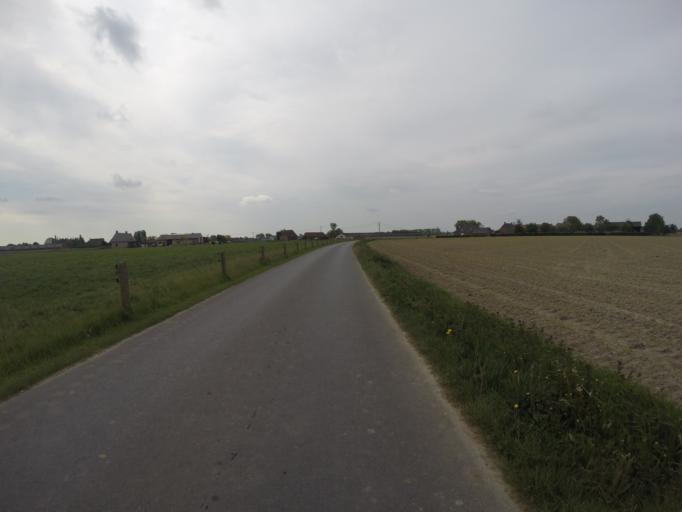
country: BE
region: Flanders
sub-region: Provincie West-Vlaanderen
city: Tielt
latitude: 51.0411
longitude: 3.3211
